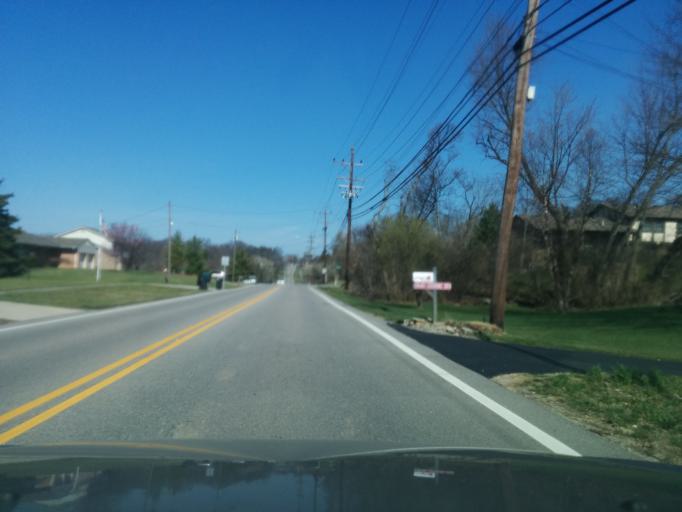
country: US
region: Ohio
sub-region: Hamilton County
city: Dent
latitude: 39.1888
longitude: -84.6278
